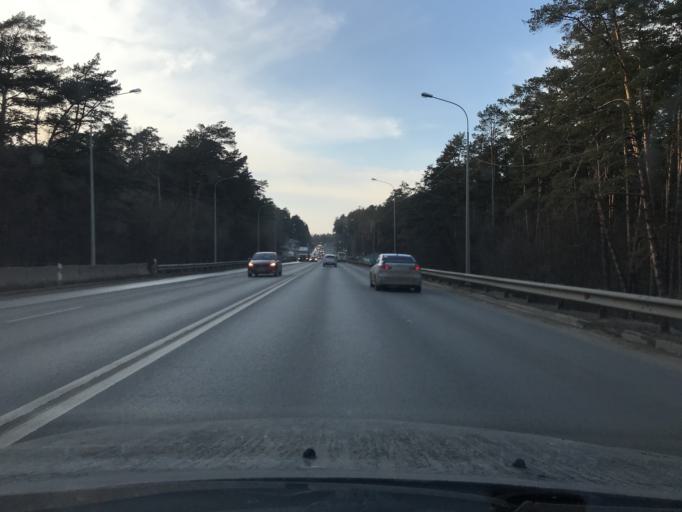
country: RU
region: Kaluga
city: Kaluga
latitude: 54.5155
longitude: 36.2057
